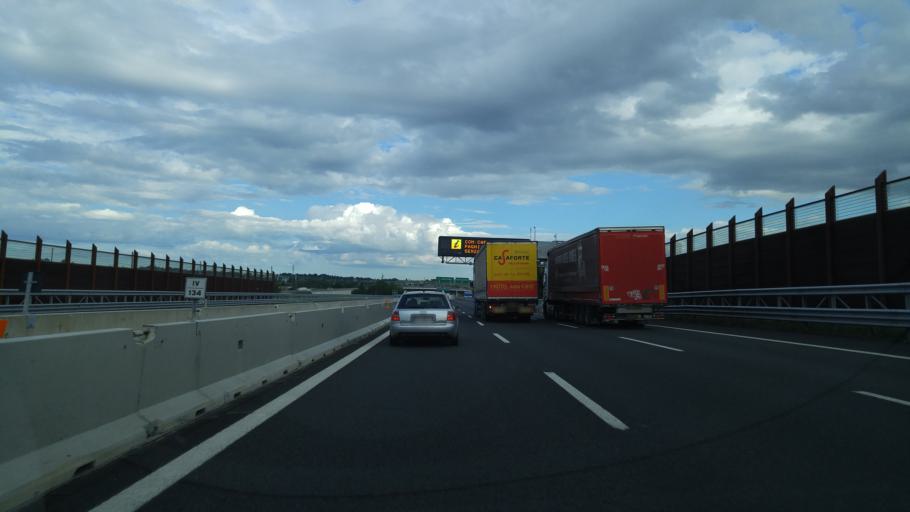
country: IT
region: Emilia-Romagna
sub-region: Provincia di Rimini
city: Riccione
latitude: 43.9907
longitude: 12.6274
